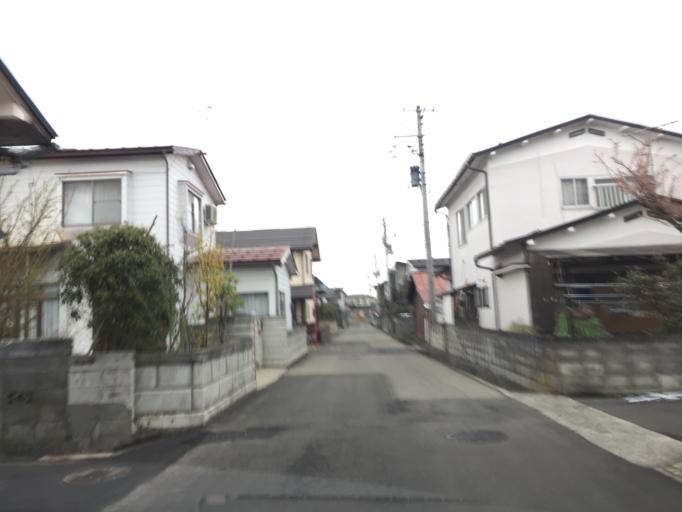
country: JP
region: Fukushima
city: Kitakata
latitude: 37.4992
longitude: 139.9168
